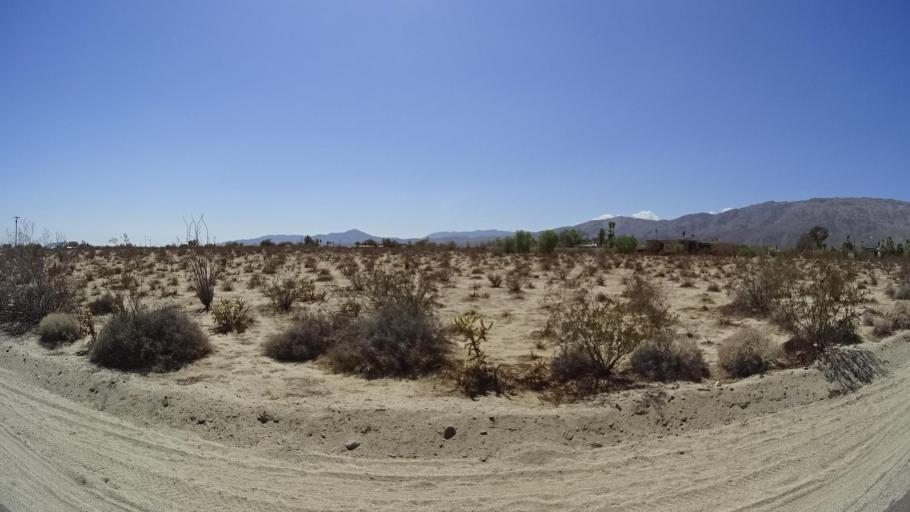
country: US
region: California
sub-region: San Diego County
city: Borrego Springs
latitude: 33.2373
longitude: -116.3777
